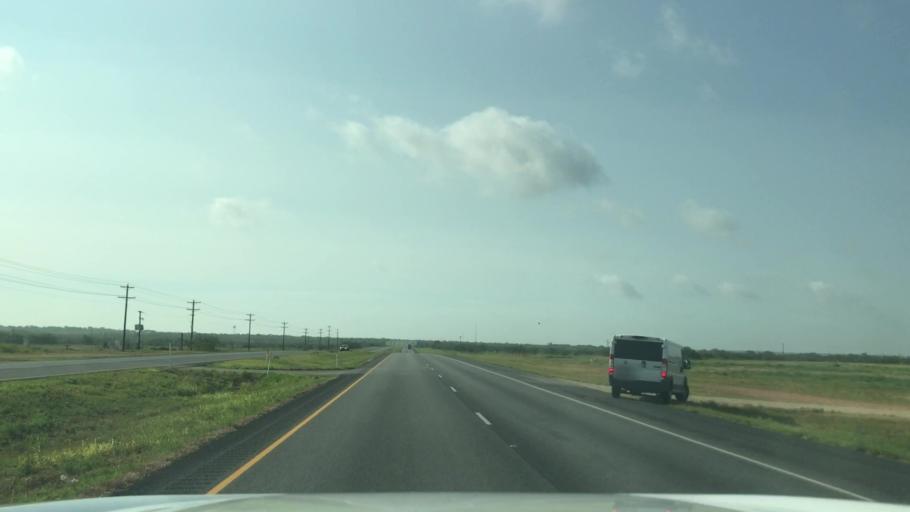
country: US
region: Texas
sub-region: Scurry County
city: Snyder
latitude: 32.7750
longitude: -100.9412
